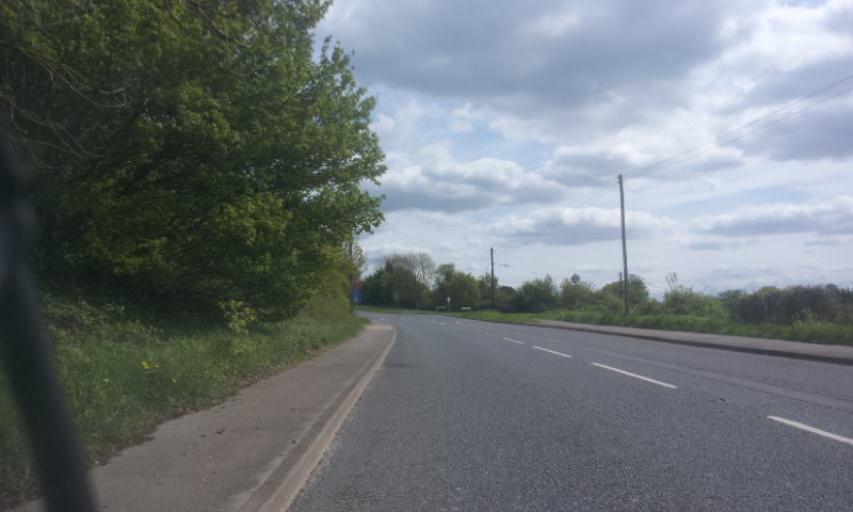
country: GB
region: England
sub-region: Kent
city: Longfield
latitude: 51.3908
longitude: 0.3282
